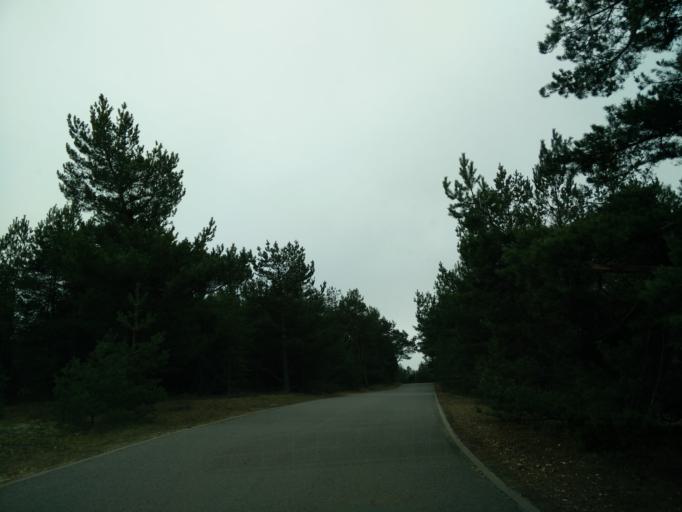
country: LT
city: Nida
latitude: 55.2968
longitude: 20.9860
